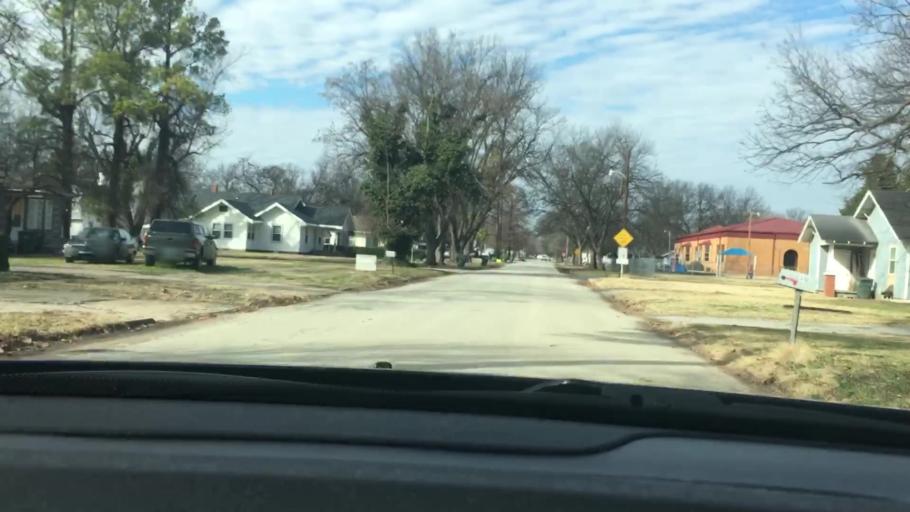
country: US
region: Oklahoma
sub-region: Garvin County
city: Pauls Valley
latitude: 34.7397
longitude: -97.2121
